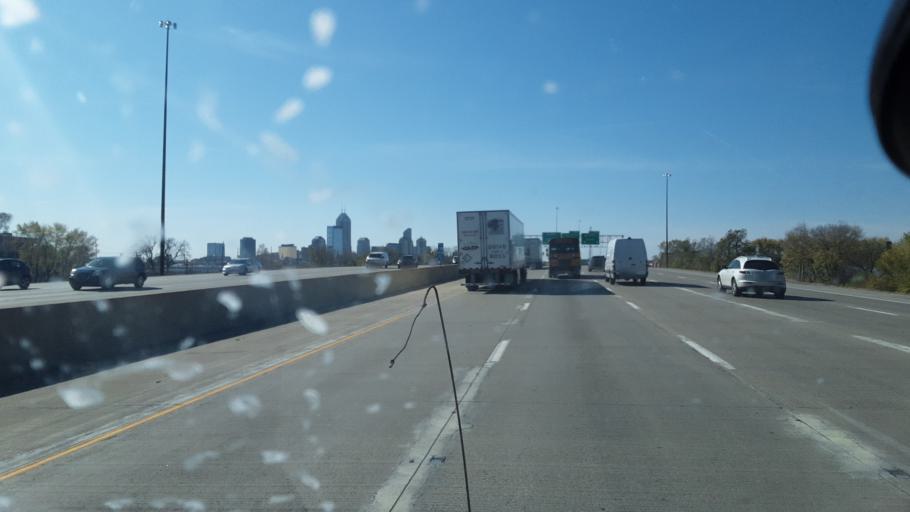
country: US
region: Indiana
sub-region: Marion County
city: Indianapolis
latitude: 39.7876
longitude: -86.1356
